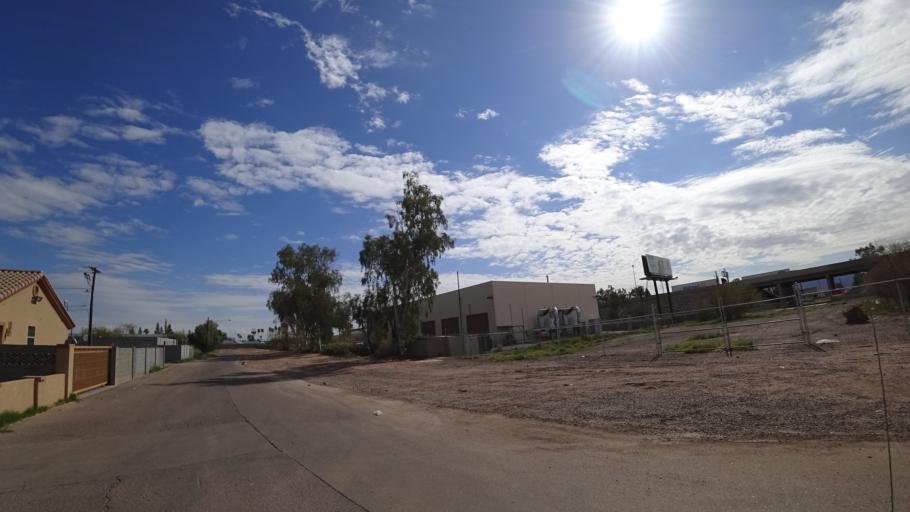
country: US
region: Arizona
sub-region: Maricopa County
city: Phoenix
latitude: 33.4296
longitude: -112.0695
